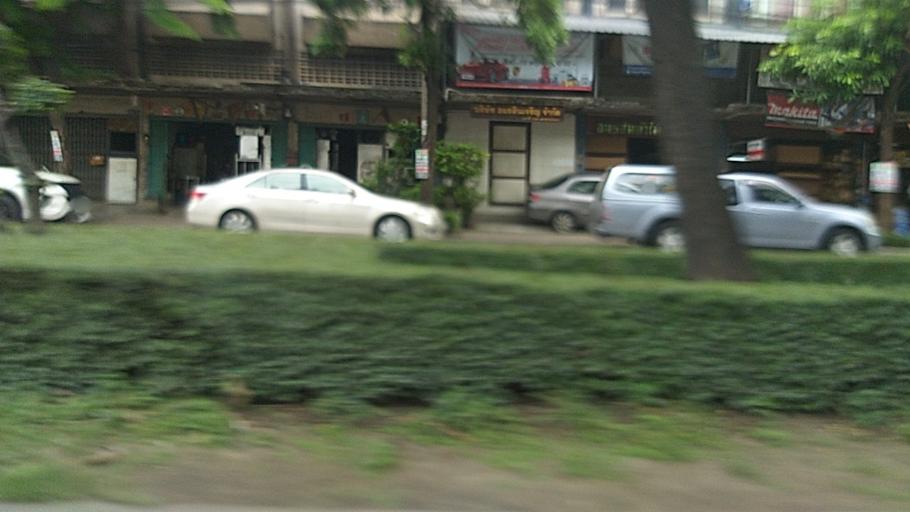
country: TH
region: Bangkok
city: Suan Luang
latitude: 13.7252
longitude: 100.6576
